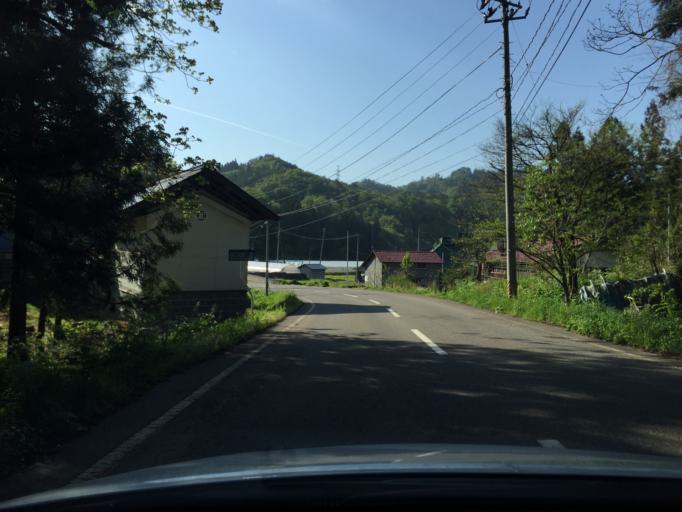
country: JP
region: Fukushima
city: Kitakata
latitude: 37.6720
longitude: 139.7831
